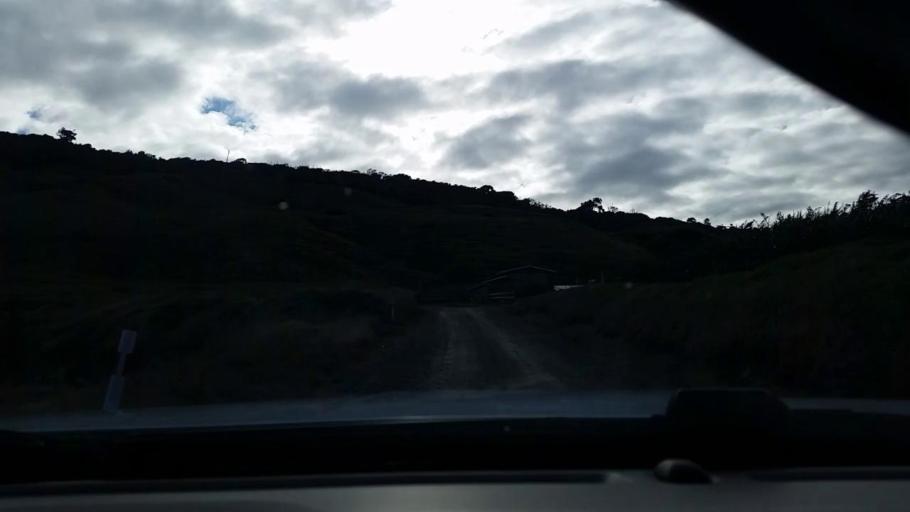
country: NZ
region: Southland
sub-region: Southland District
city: Riverton
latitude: -46.3309
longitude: 167.7125
